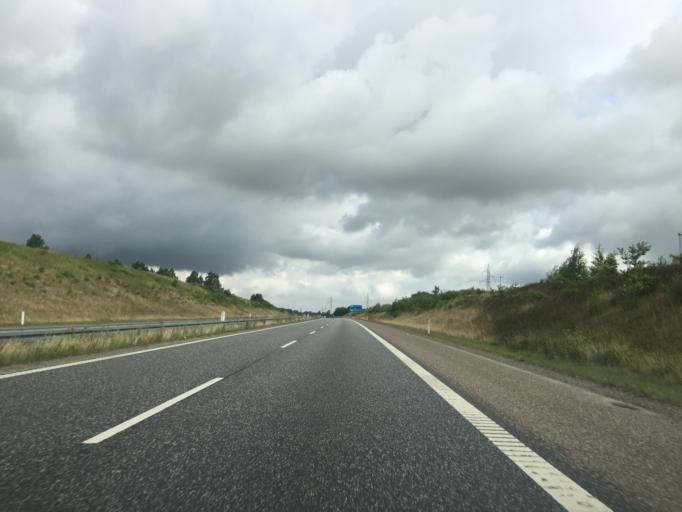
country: DK
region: South Denmark
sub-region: Faaborg-Midtfyn Kommune
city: Ringe
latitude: 55.1703
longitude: 10.5416
